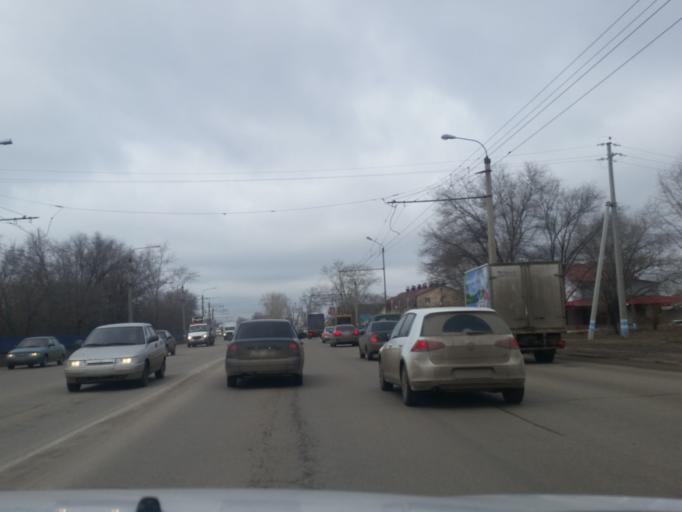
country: RU
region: Ulyanovsk
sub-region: Ulyanovskiy Rayon
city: Ulyanovsk
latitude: 54.3371
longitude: 48.5405
